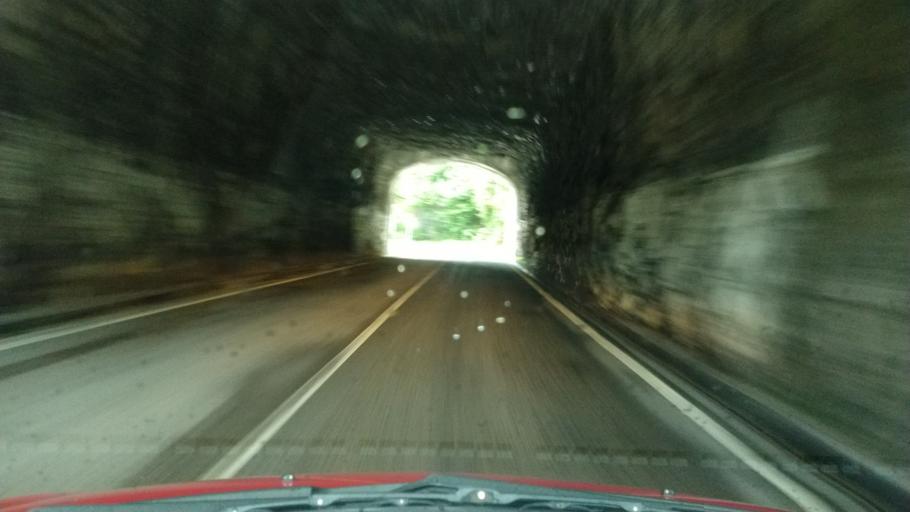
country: IT
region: Veneto
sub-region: Provincia di Vicenza
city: Arsiero
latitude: 45.8226
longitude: 11.3621
